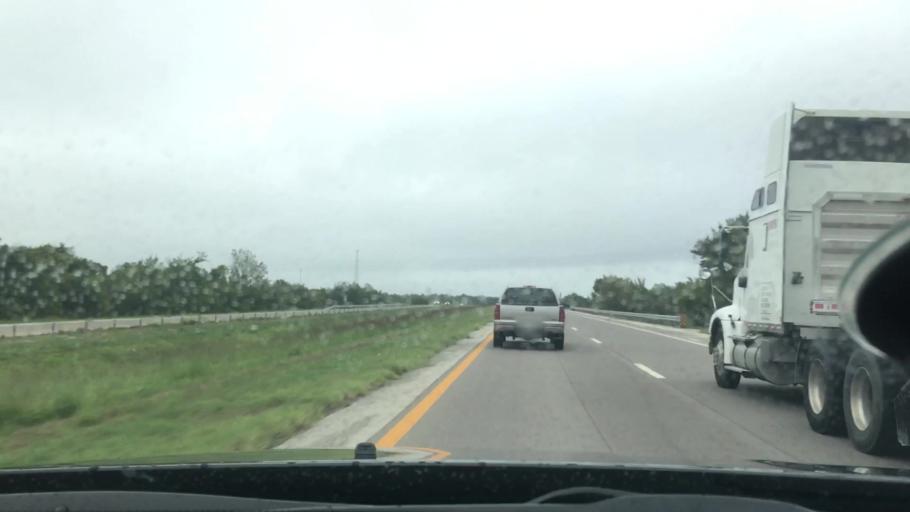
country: US
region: Oklahoma
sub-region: Okfuskee County
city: Okemah
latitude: 35.4283
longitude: -96.2134
